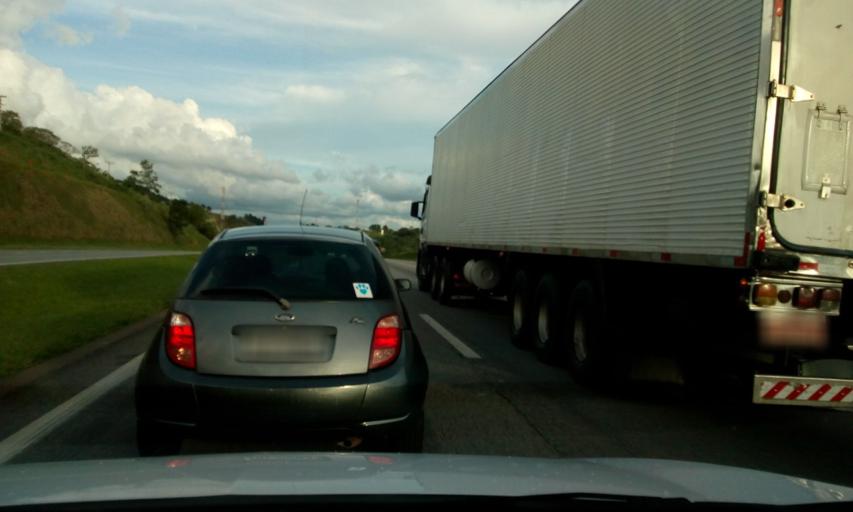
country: BR
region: Sao Paulo
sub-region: Atibaia
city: Atibaia
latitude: -23.0985
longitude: -46.6153
